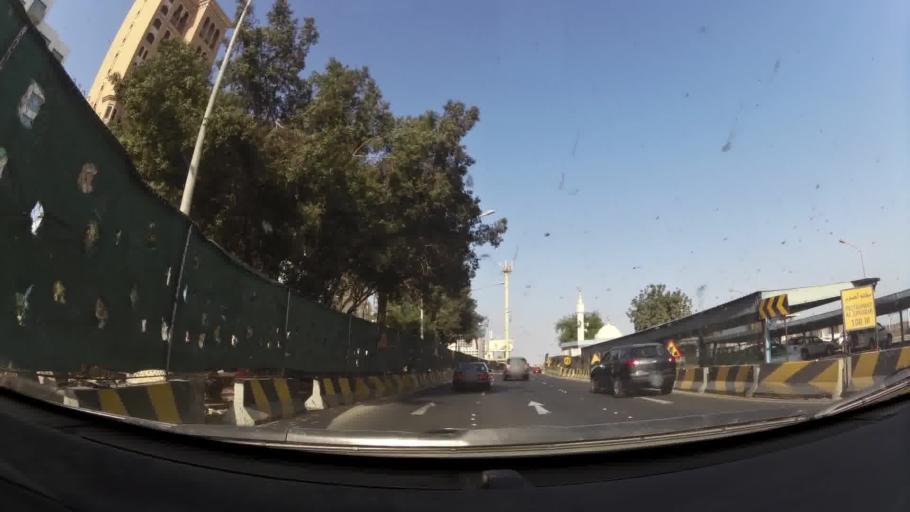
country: KW
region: Muhafazat Hawalli
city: As Salimiyah
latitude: 29.3266
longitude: 48.0904
